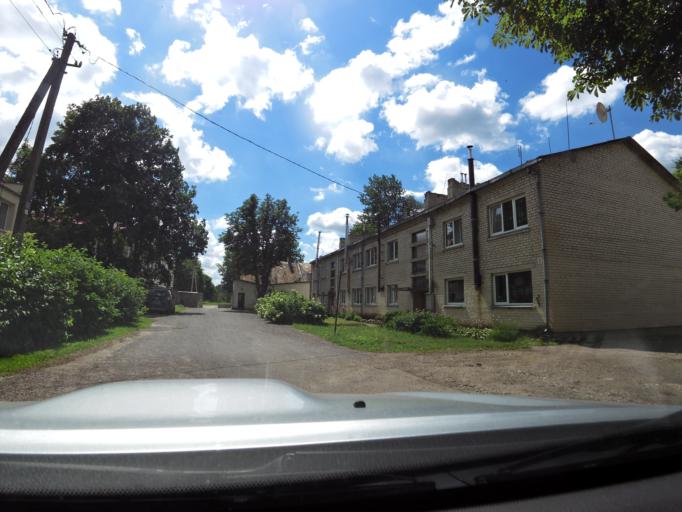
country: LT
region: Vilnius County
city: Elektrenai
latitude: 54.9532
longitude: 24.6552
